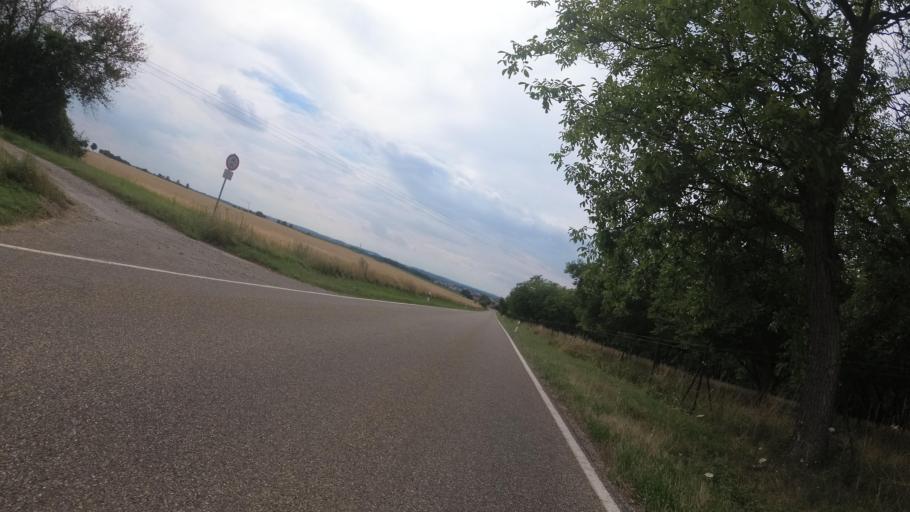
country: DE
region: Baden-Wuerttemberg
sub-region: Regierungsbezirk Stuttgart
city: Oedheim
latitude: 49.2507
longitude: 9.2259
